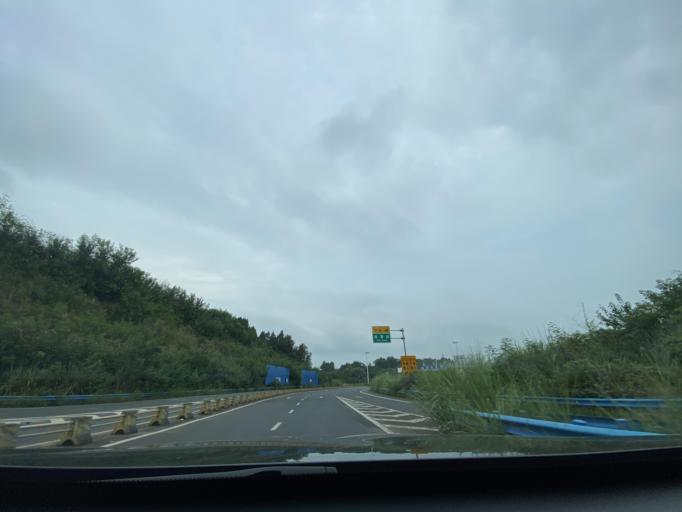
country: CN
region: Sichuan
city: Jiancheng
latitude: 30.5006
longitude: 104.4453
